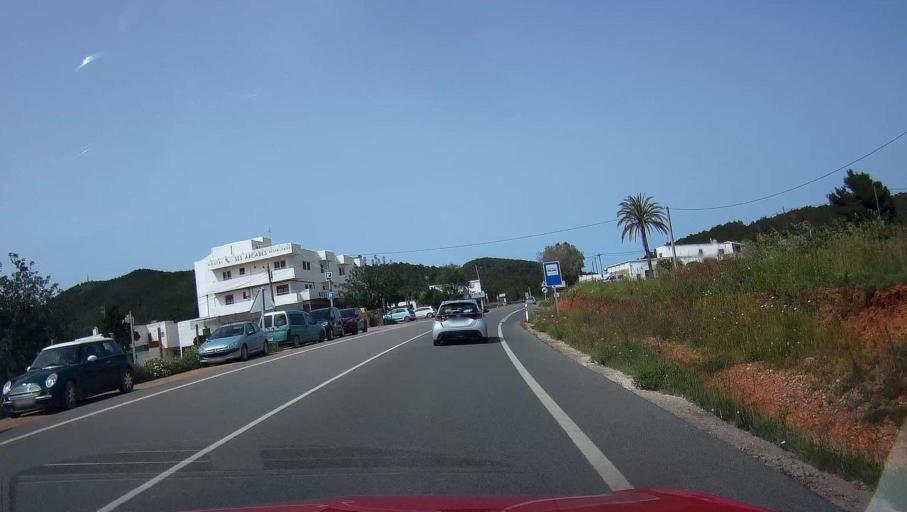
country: ES
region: Balearic Islands
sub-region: Illes Balears
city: Sant Joan de Labritja
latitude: 39.0662
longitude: 1.4944
